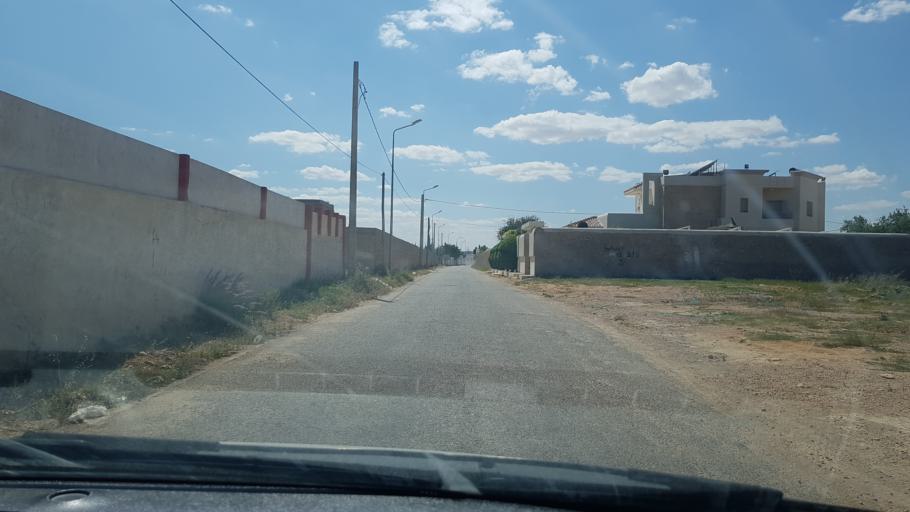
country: TN
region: Safaqis
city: Al Qarmadah
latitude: 34.8290
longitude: 10.7628
